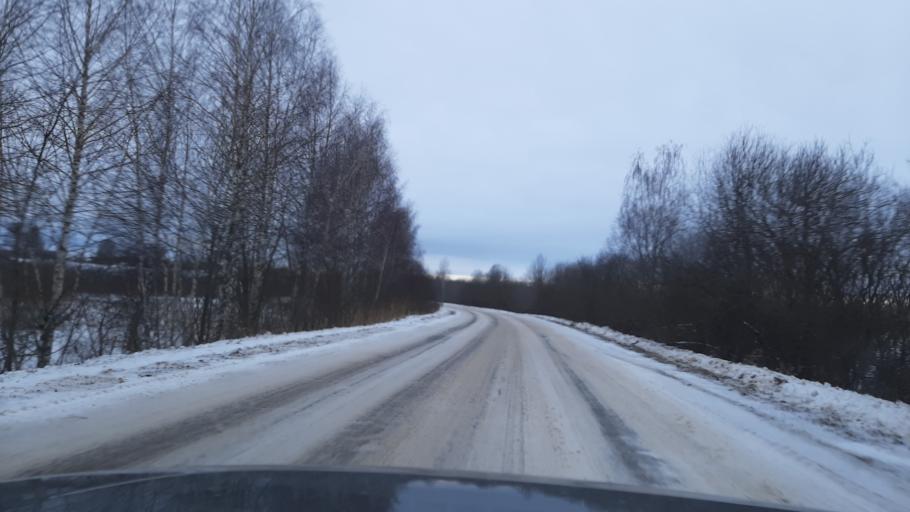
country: RU
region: Kostroma
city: Volgorechensk
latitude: 57.4401
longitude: 41.1016
